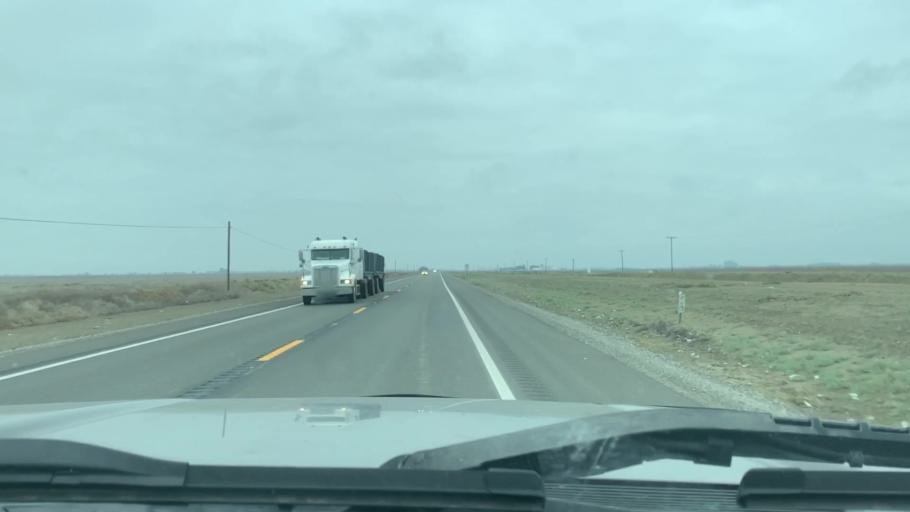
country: US
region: California
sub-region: Kings County
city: Stratford
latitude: 36.1433
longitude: -119.8723
